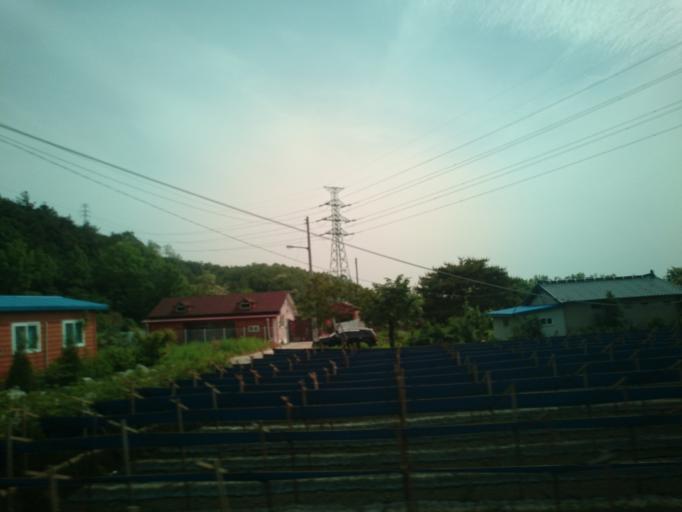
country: KR
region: Jeollabuk-do
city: Wanju
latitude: 35.9000
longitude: 127.1958
